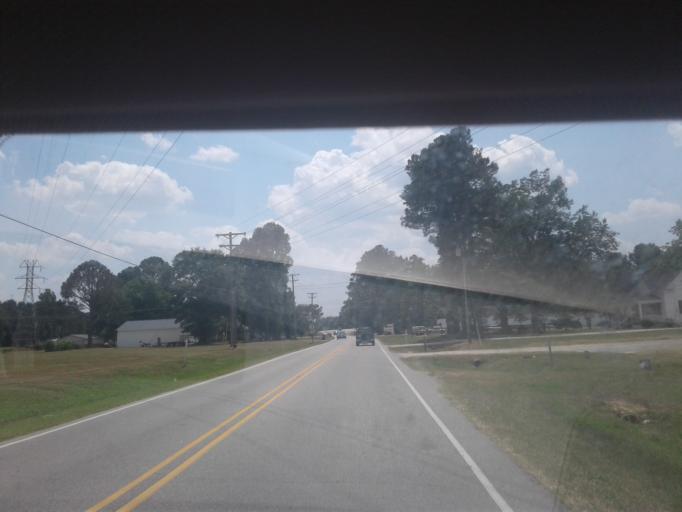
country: US
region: North Carolina
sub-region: Harnett County
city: Erwin
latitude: 35.3312
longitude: -78.6576
